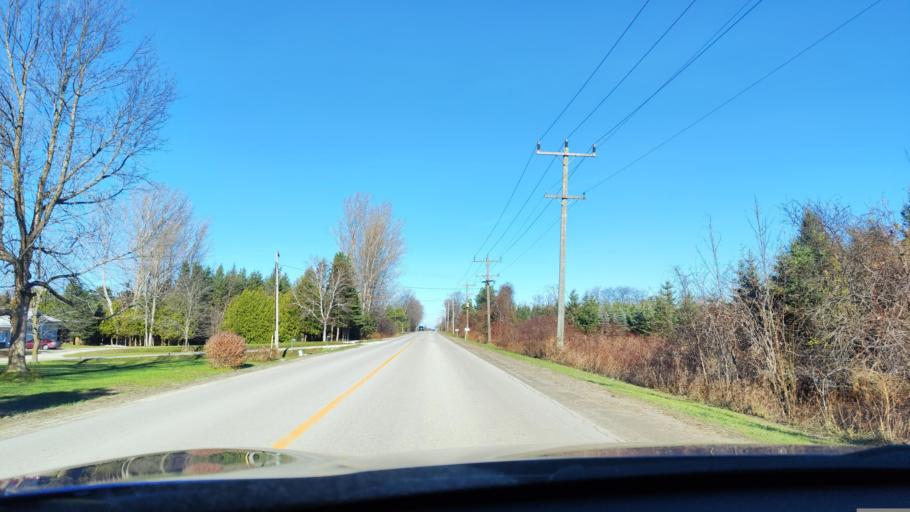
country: CA
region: Ontario
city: Collingwood
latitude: 44.4728
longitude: -80.1755
